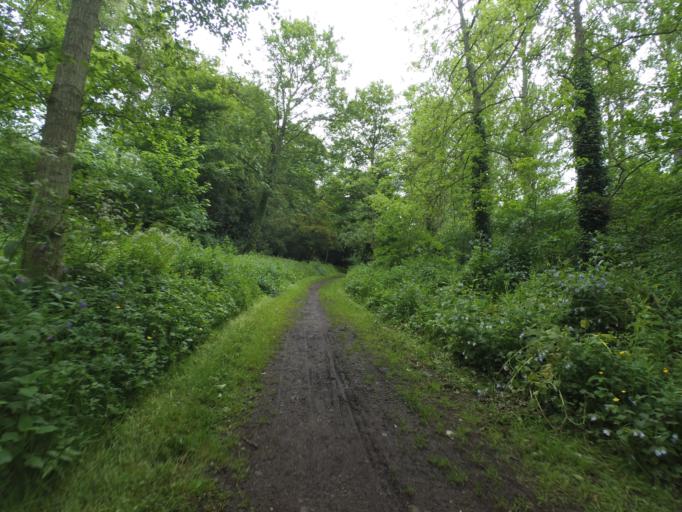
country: GB
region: Scotland
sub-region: East Lothian
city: Pencaitland
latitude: 55.9136
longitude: -2.8972
